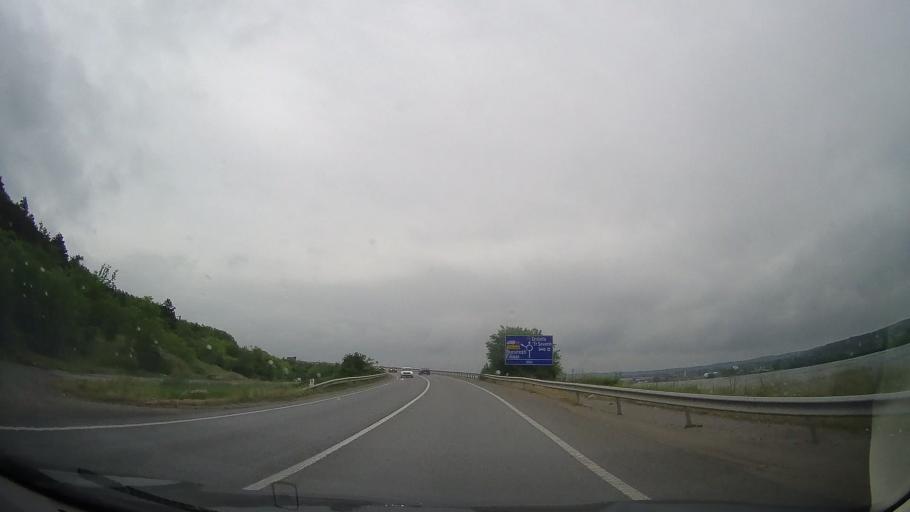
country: RO
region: Mehedinti
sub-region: Municipiul Drobeta-Turnu Severin
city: Gura Vaii
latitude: 44.6379
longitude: 22.5816
